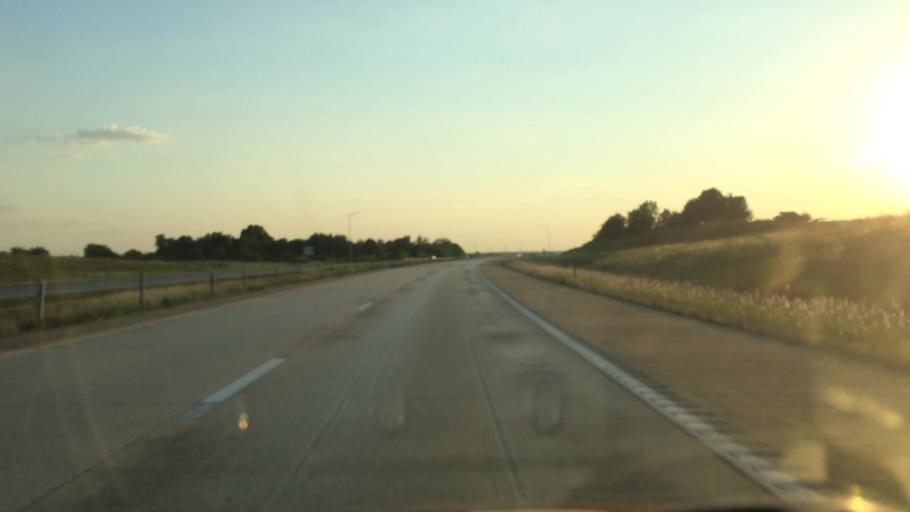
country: US
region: Missouri
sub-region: Greene County
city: Strafford
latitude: 37.2505
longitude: -93.1840
